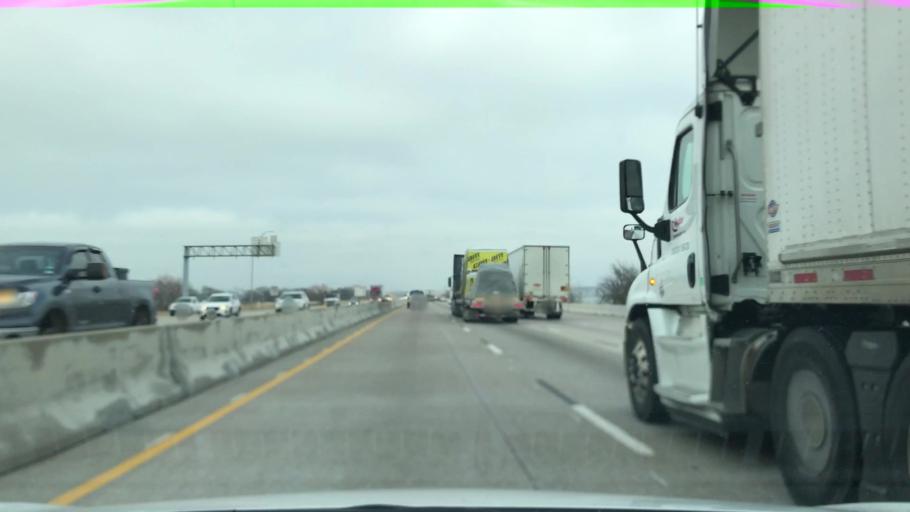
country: US
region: Texas
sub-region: Dallas County
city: Rowlett
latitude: 32.8781
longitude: -96.5145
